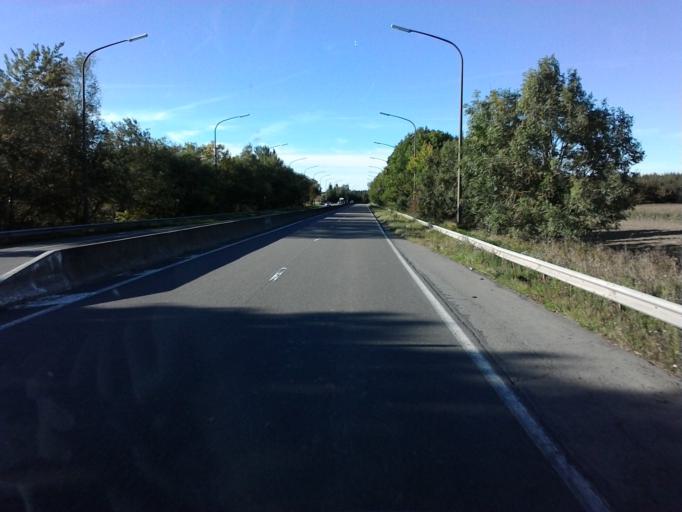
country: BE
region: Wallonia
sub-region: Province du Luxembourg
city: Fauvillers
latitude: 49.8780
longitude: 5.7057
